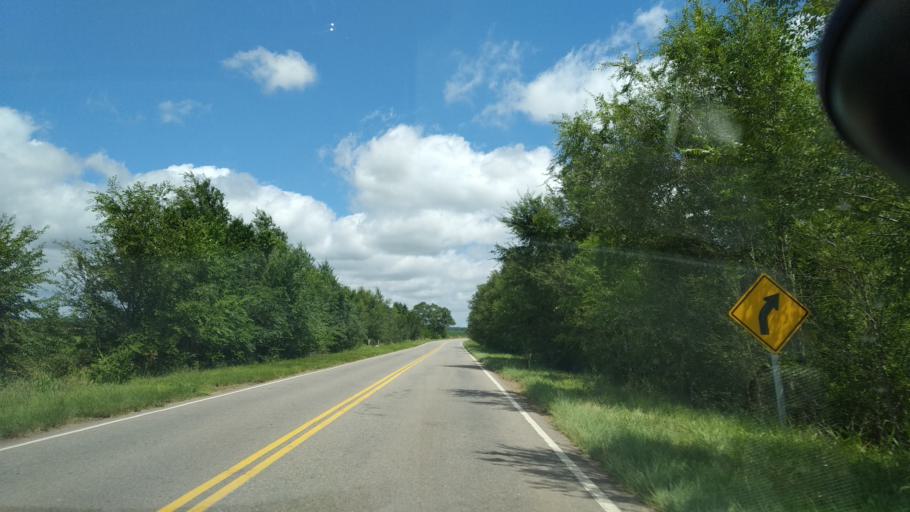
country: AR
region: Cordoba
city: Villa Cura Brochero
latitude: -31.6702
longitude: -65.0948
